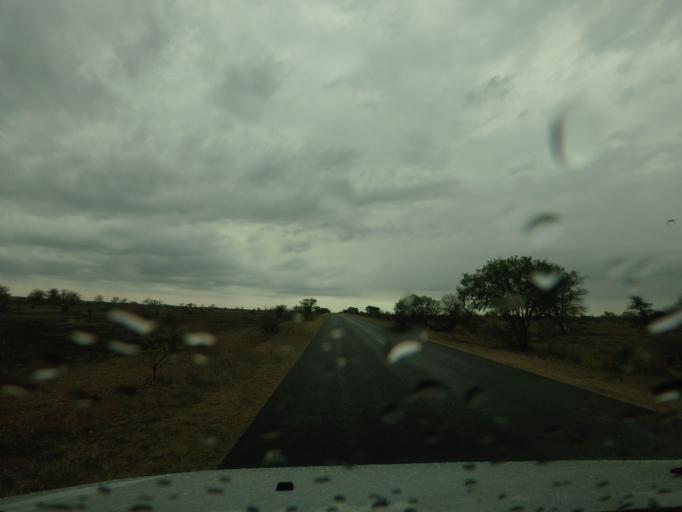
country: ZA
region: Limpopo
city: Thulamahashi
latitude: -24.4752
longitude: 31.3994
